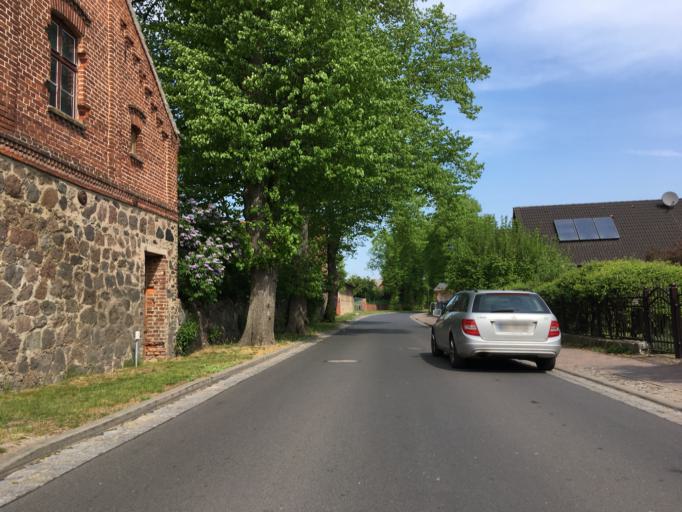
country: DE
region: Brandenburg
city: Werneuchen
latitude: 52.6024
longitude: 13.7564
